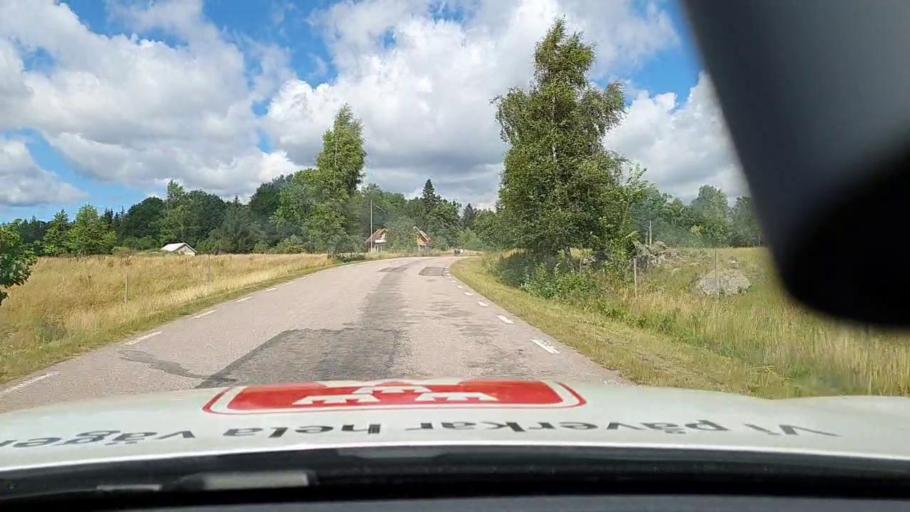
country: SE
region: Vaestra Goetaland
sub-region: Karlsborgs Kommun
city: Molltorp
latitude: 58.6018
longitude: 14.2783
